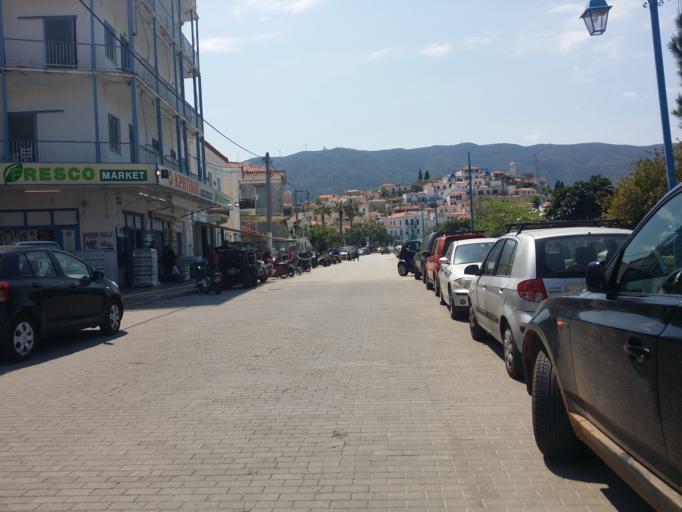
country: GR
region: Attica
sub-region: Nomos Piraios
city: Poros
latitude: 37.5021
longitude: 23.4550
